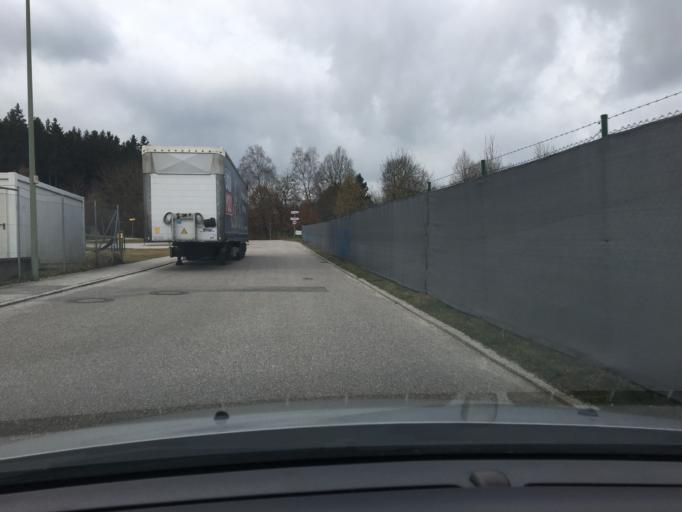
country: DE
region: Bavaria
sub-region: Lower Bavaria
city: Vilsbiburg
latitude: 48.4482
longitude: 12.3388
